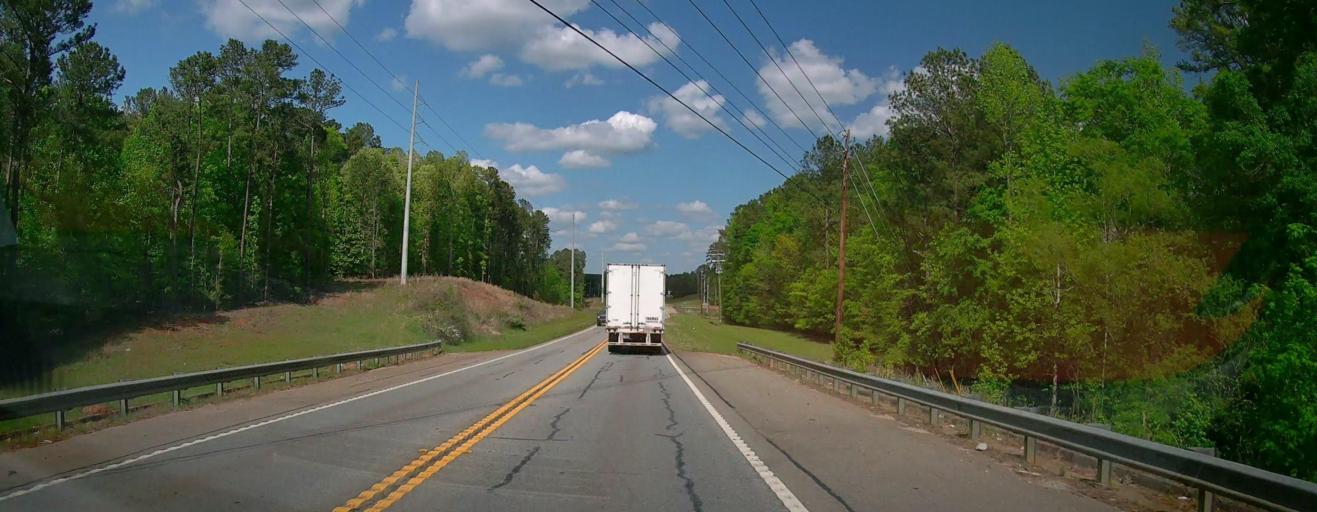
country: US
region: Georgia
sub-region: Putnam County
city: Jefferson
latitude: 33.4863
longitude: -83.2304
